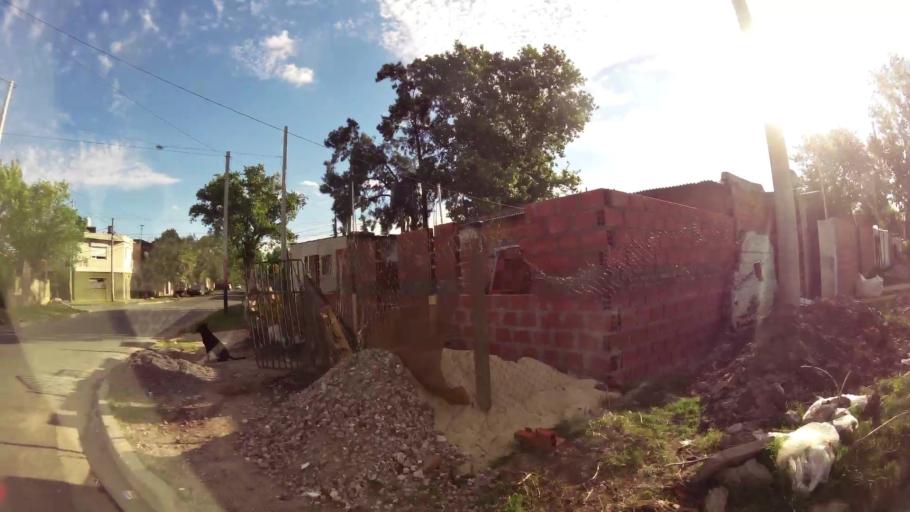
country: AR
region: Santa Fe
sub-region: Departamento de Rosario
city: Rosario
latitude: -32.9857
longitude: -60.6682
